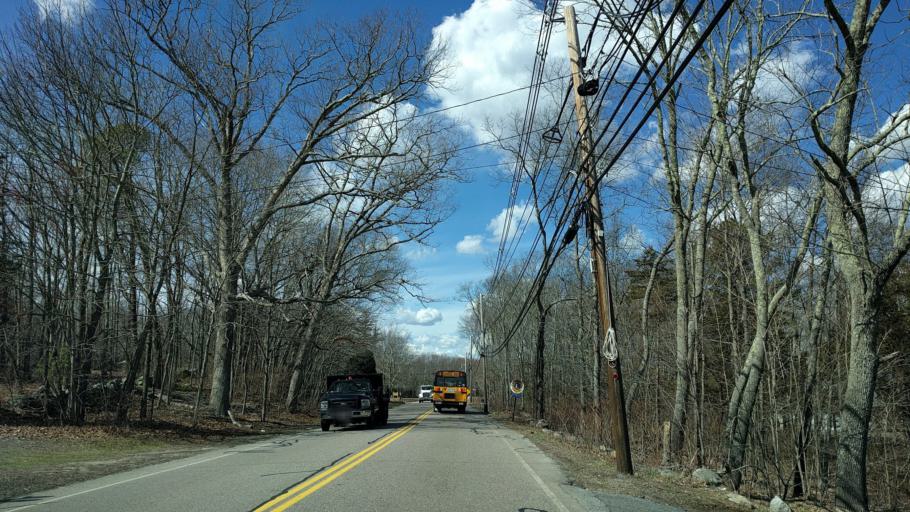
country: US
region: Massachusetts
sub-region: Worcester County
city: Mendon
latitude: 42.0946
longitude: -71.5368
